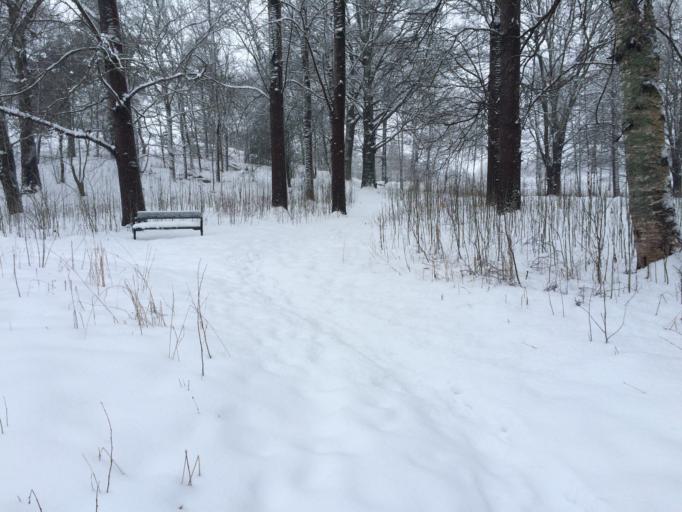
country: SE
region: Vaestmanland
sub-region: Hallstahammars Kommun
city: Hallstahammar
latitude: 59.6133
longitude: 16.2130
